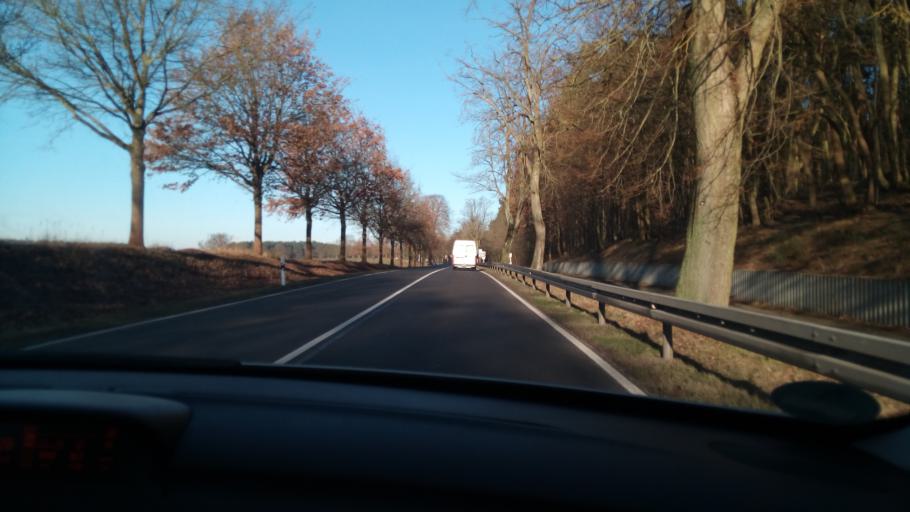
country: DE
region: Mecklenburg-Vorpommern
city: Rechlin
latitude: 53.2863
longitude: 12.7953
